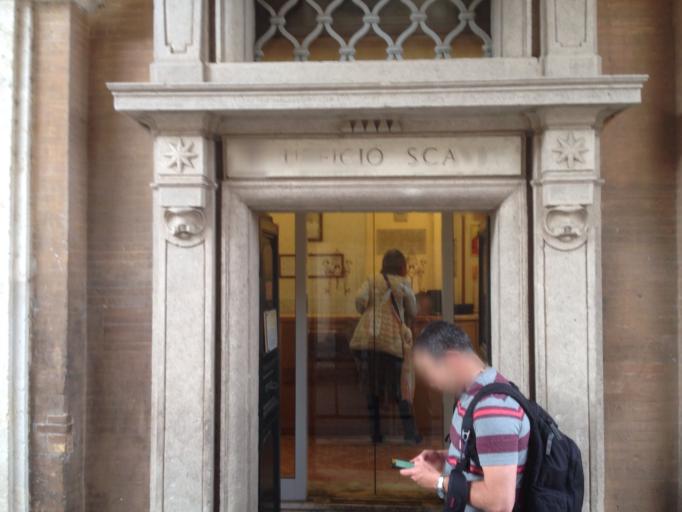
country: VA
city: Vatican City
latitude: 41.9017
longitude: 12.4540
